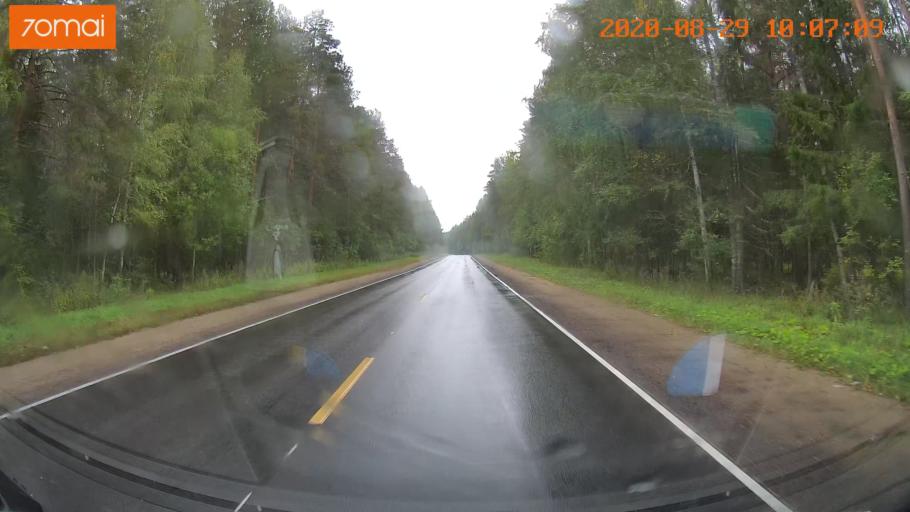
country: RU
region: Ivanovo
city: Kuznechikha
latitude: 57.3834
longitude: 42.5608
